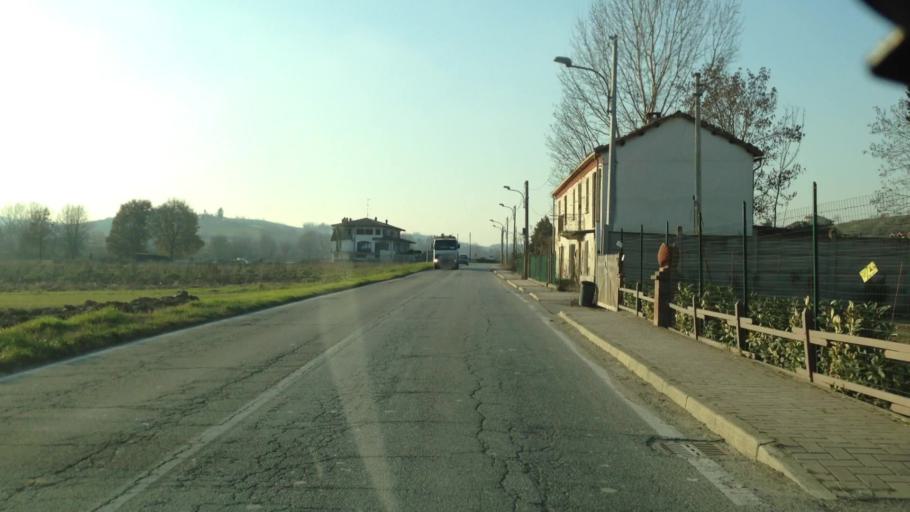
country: IT
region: Piedmont
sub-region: Provincia di Asti
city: Montaldo Scarampi
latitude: 44.8165
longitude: 8.2535
